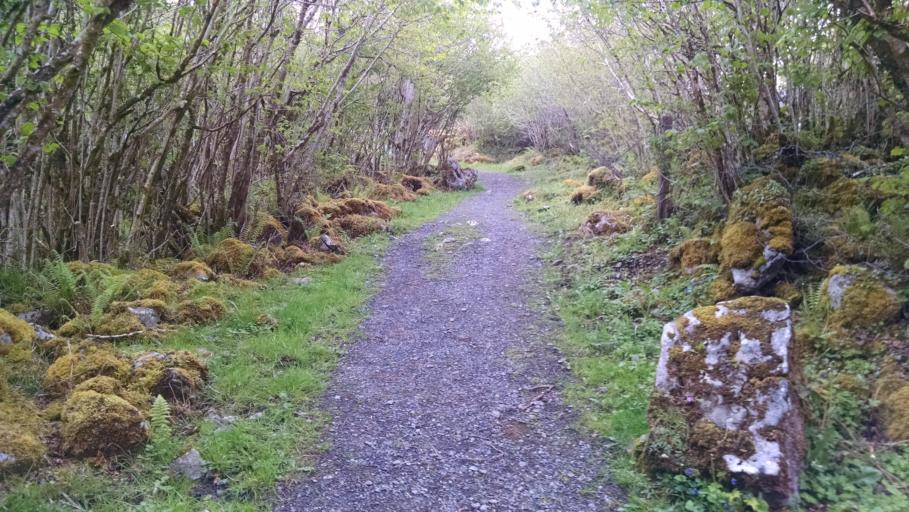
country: IE
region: Munster
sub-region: An Clar
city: Ennis
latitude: 53.0118
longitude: -9.0744
